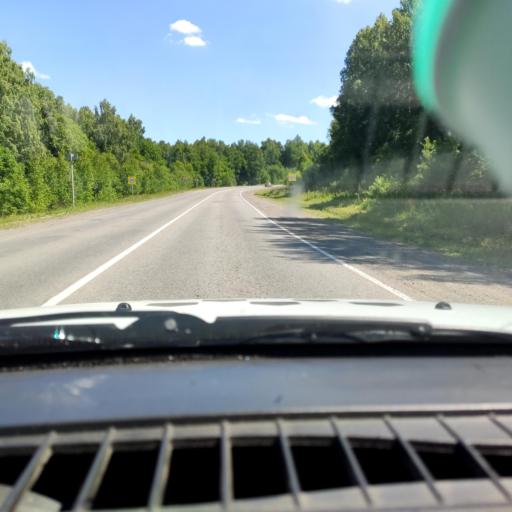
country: RU
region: Bashkortostan
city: Verkhniye Kigi
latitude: 55.3852
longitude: 58.6726
